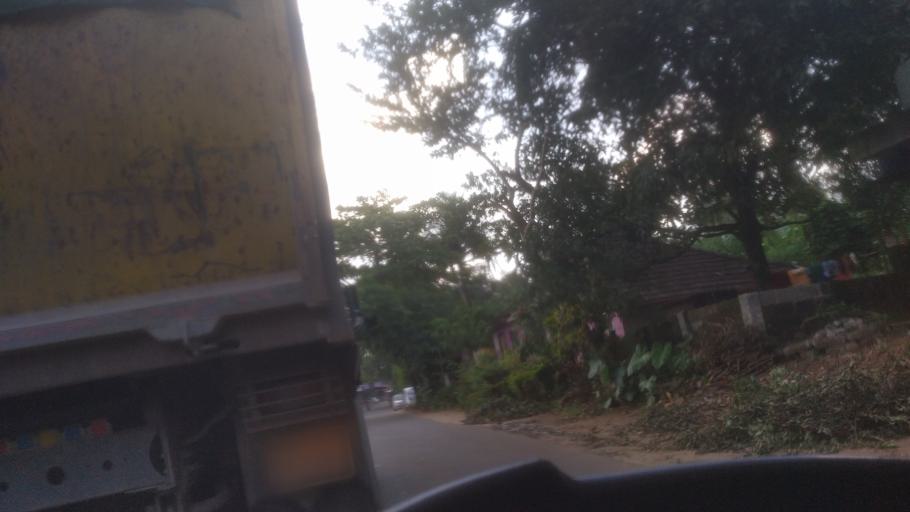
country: IN
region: Kerala
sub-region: Ernakulam
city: Kotamangalam
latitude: 10.0056
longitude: 76.6828
